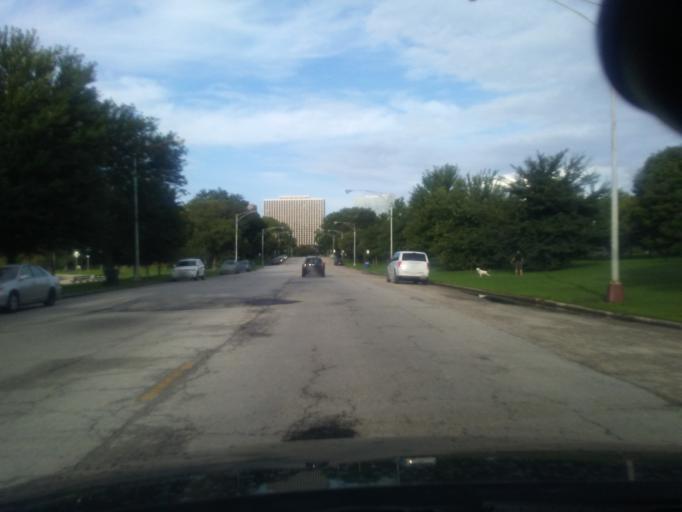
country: US
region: Illinois
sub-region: Cook County
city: Evanston
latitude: 41.9627
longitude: -87.6405
